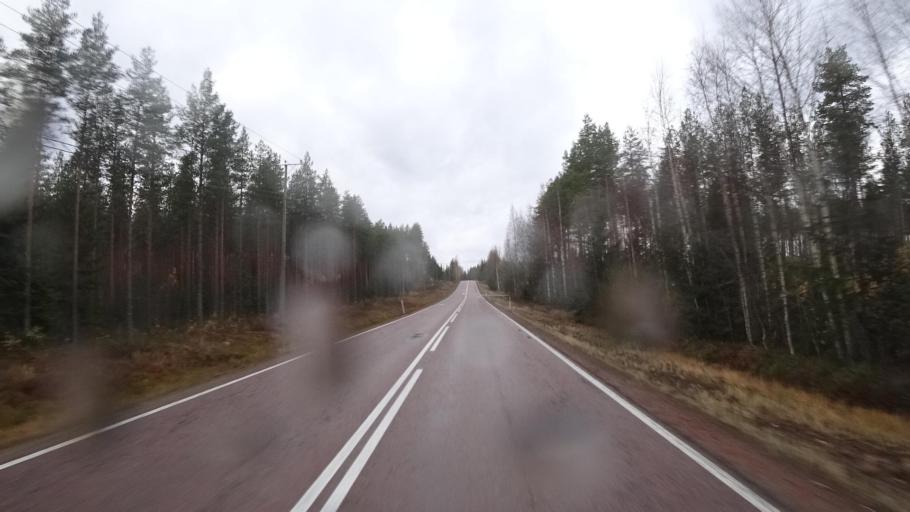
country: FI
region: Southern Savonia
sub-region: Mikkeli
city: Kangasniemi
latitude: 62.0729
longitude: 26.6815
